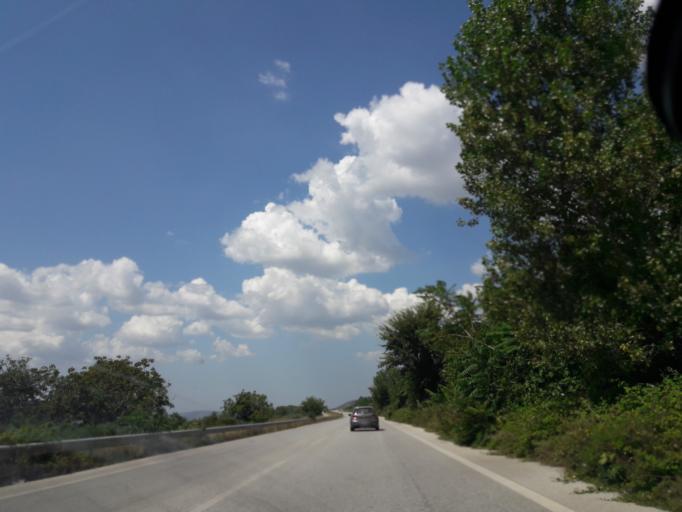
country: GR
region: Central Macedonia
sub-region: Nomos Chalkidikis
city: Galatista
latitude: 40.4619
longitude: 23.2787
